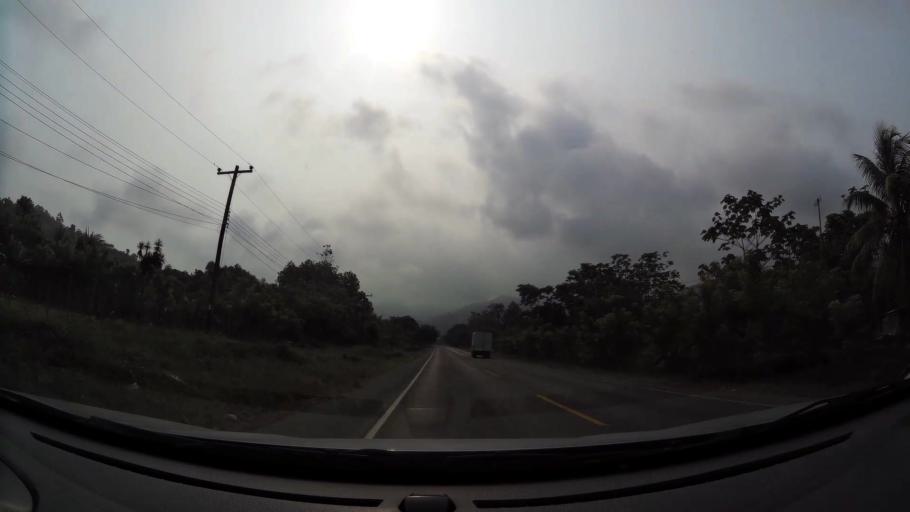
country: HN
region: Yoro
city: Toyos
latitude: 15.5546
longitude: -87.6353
